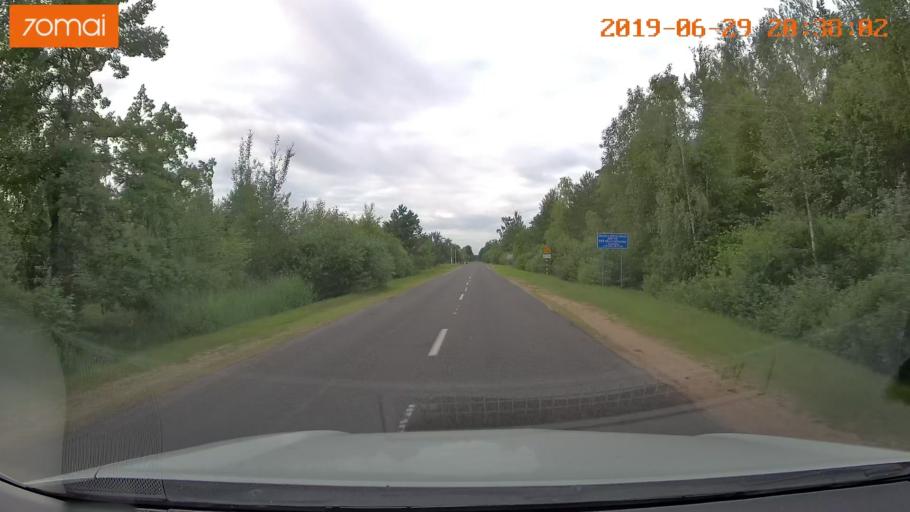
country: BY
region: Brest
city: Hantsavichy
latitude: 52.5454
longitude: 26.3653
